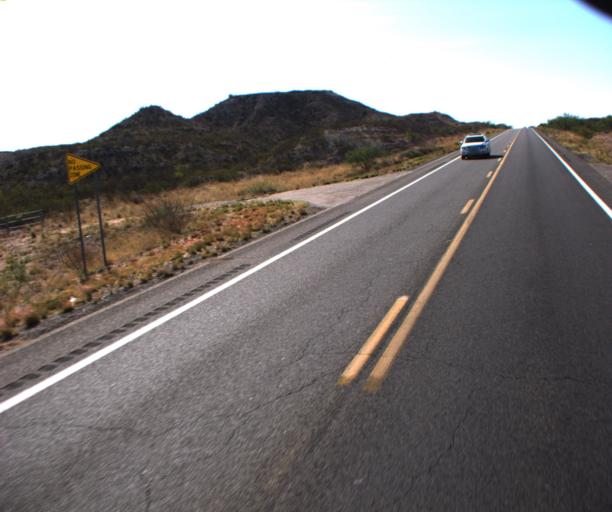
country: US
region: Arizona
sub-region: Cochise County
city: Saint David
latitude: 31.8321
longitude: -110.1823
